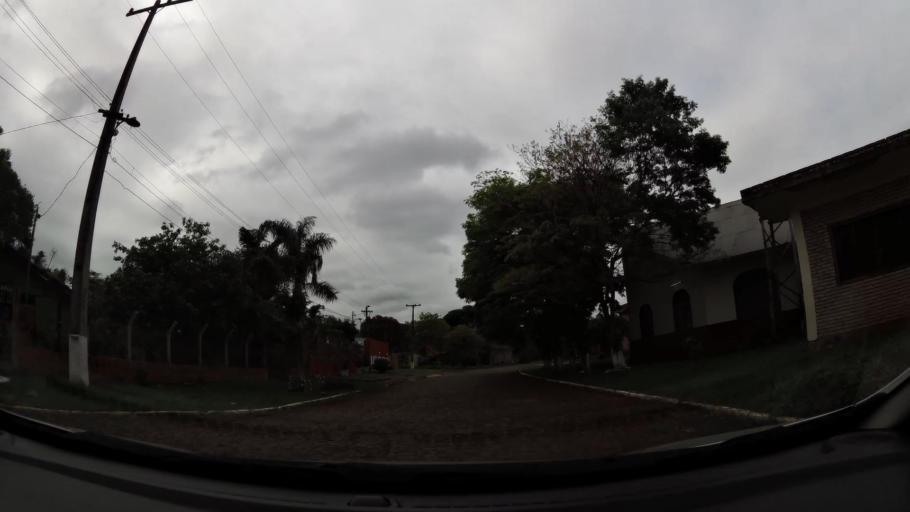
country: PY
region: Alto Parana
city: Ciudad del Este
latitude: -25.4105
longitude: -54.6367
